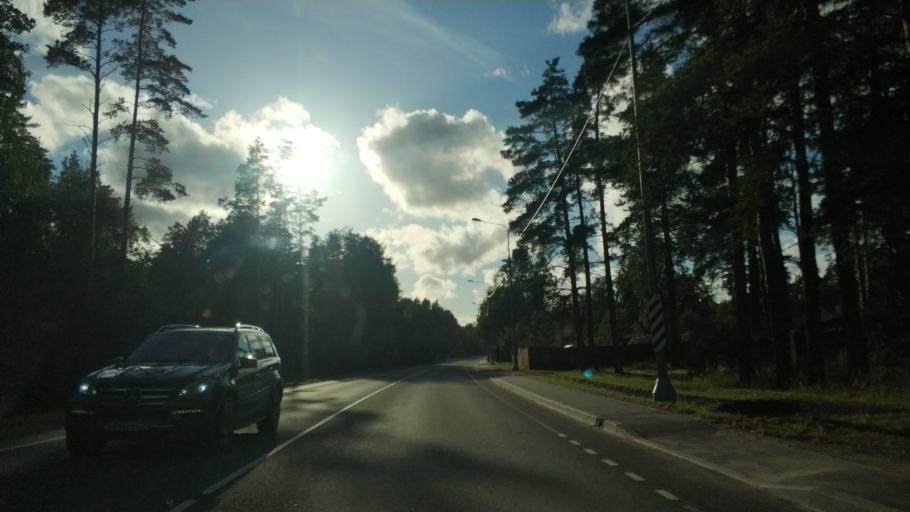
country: RU
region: Leningrad
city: Sapernoye
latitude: 60.7131
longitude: 30.0282
